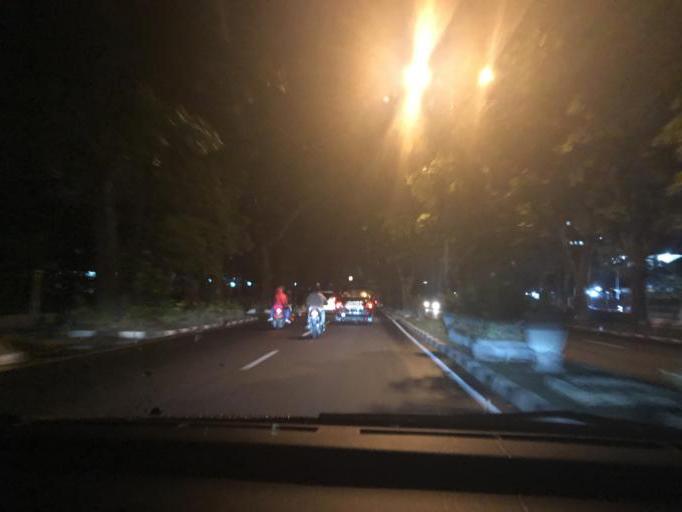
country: ID
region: West Java
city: Bandung
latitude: -6.9085
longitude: 107.6312
